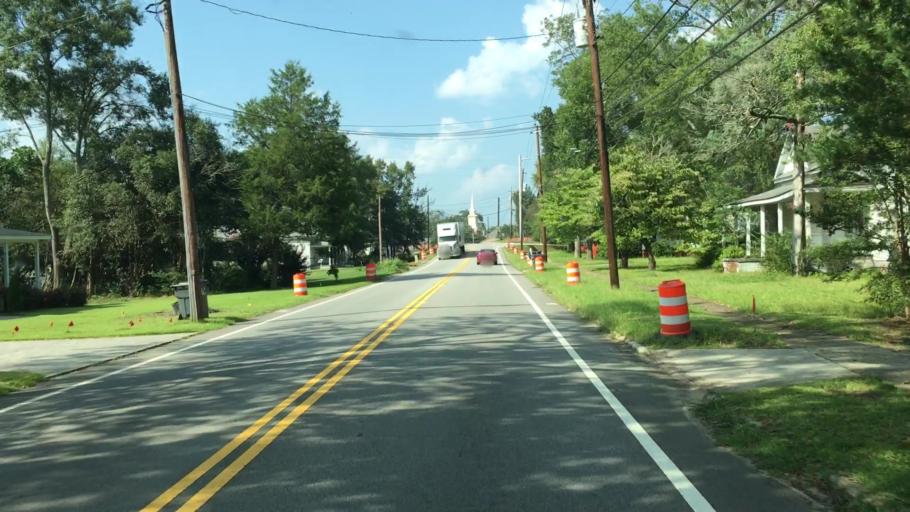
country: US
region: Georgia
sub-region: Walton County
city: Social Circle
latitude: 33.6509
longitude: -83.7217
